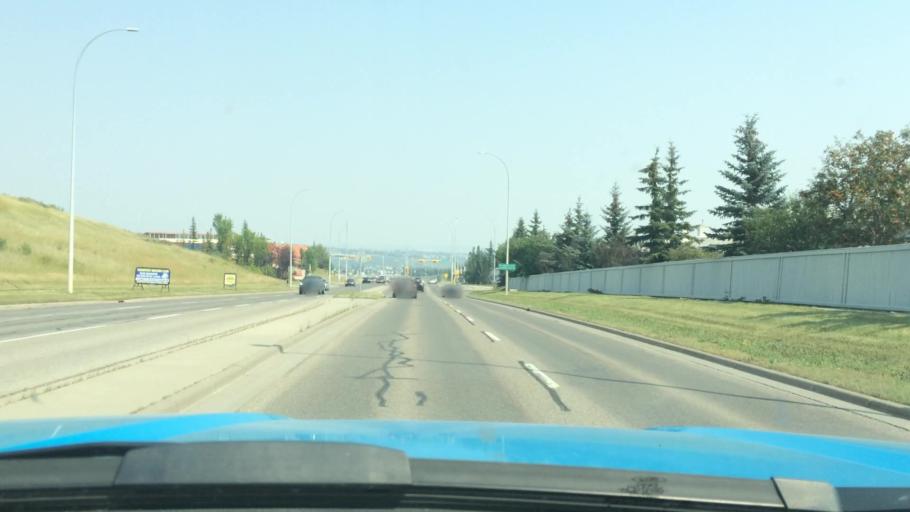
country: CA
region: Alberta
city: Calgary
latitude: 51.1398
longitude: -114.1345
